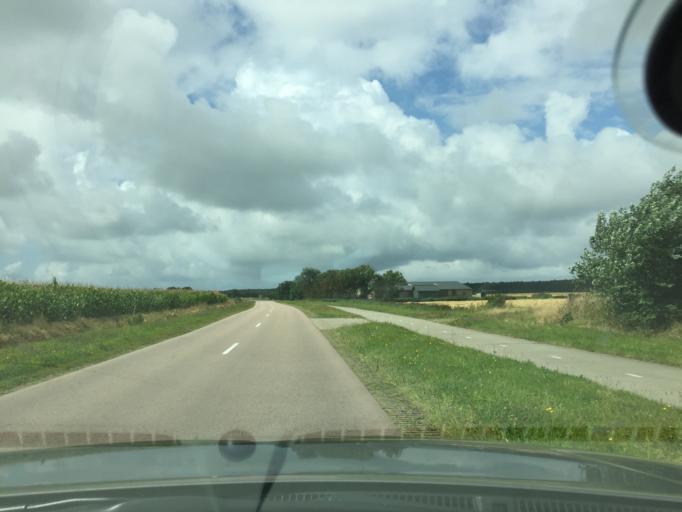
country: NL
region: North Holland
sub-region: Gemeente Texel
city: Den Burg
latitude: 53.0523
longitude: 4.7728
